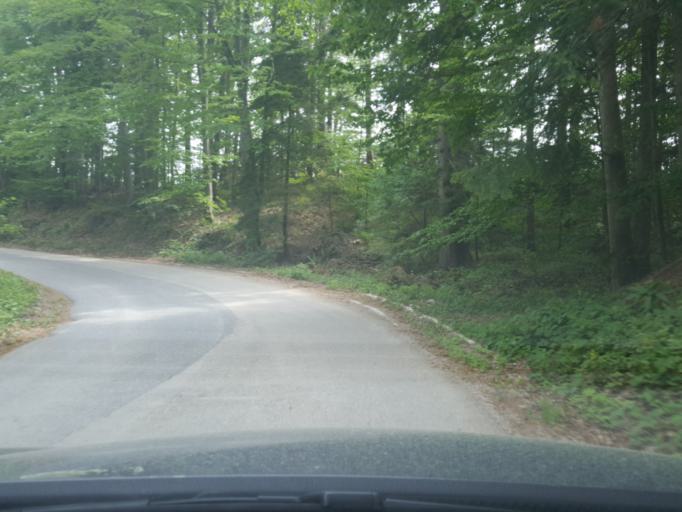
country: RS
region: Central Serbia
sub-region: Zlatiborski Okrug
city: Bajina Basta
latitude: 43.8911
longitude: 19.5292
